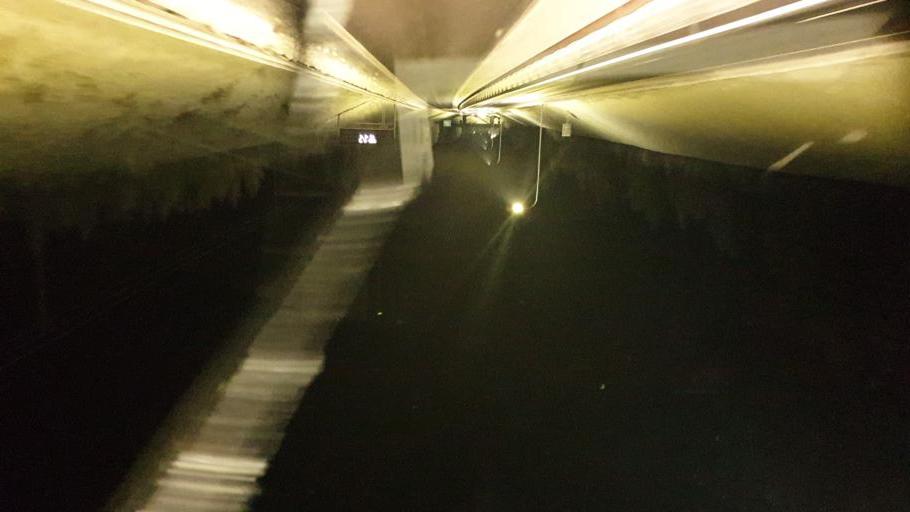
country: FI
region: Northern Ostrobothnia
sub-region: Oulu
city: Haukipudas
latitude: 65.2140
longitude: 25.4046
